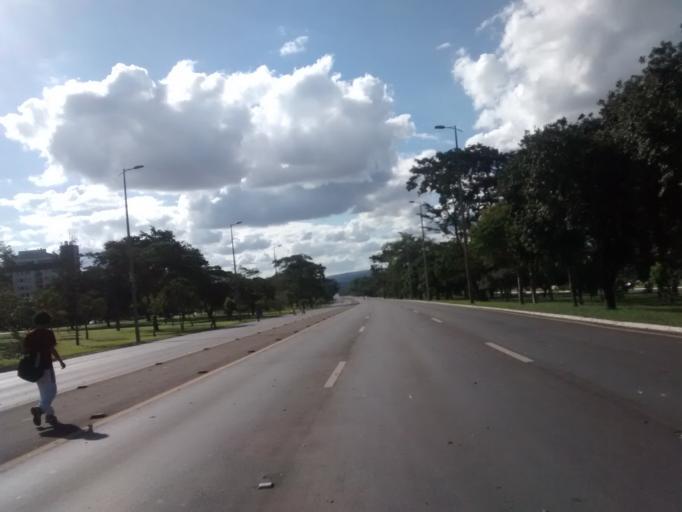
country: BR
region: Federal District
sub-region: Brasilia
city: Brasilia
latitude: -15.7689
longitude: -47.8821
